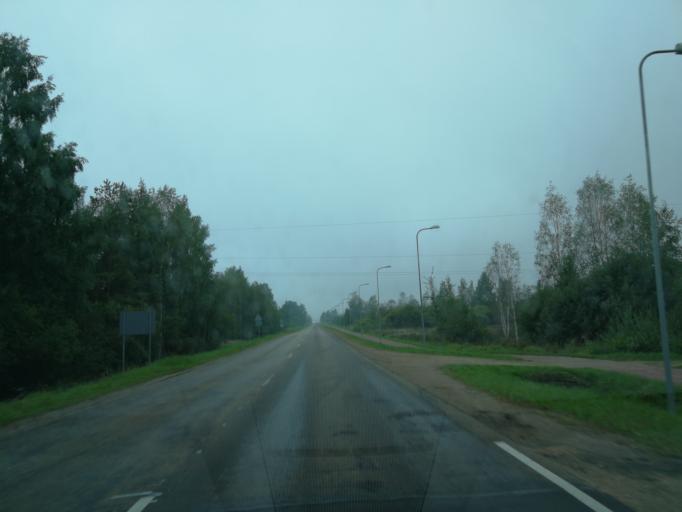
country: LV
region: Preilu Rajons
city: Preili
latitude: 56.2987
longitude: 26.7016
